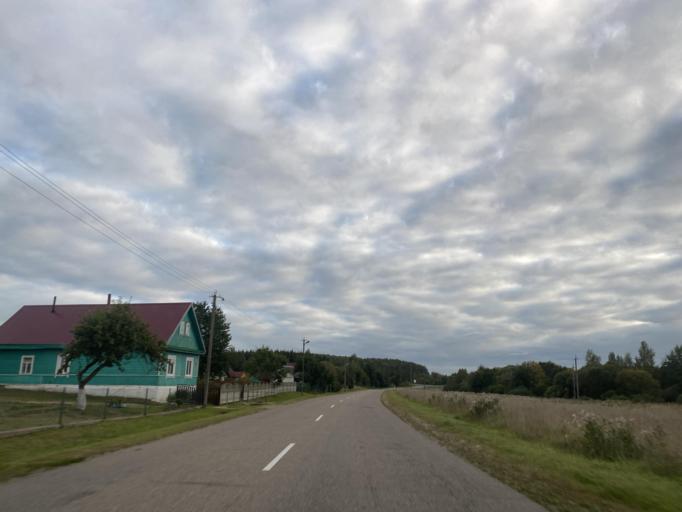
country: BY
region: Grodnenskaya
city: Kreva
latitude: 54.3012
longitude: 26.2766
